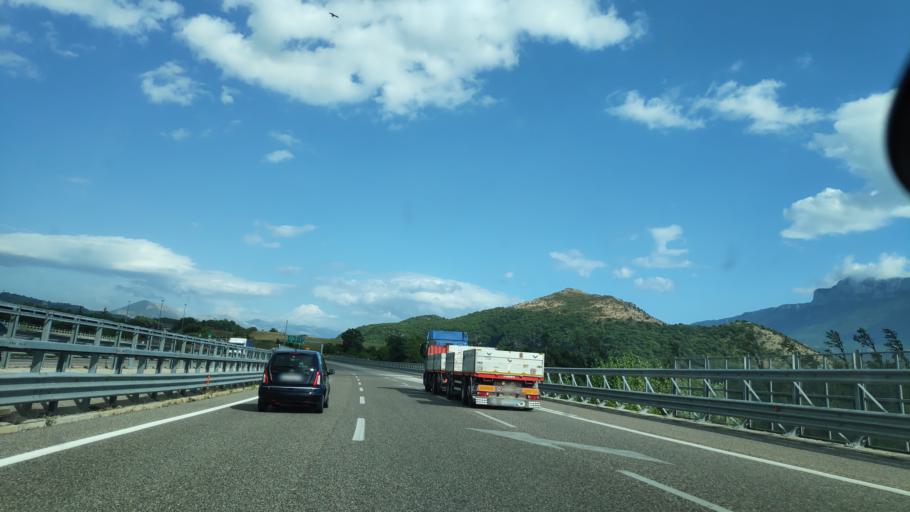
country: IT
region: Campania
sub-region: Provincia di Salerno
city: Palomonte
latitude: 40.6115
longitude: 15.2841
